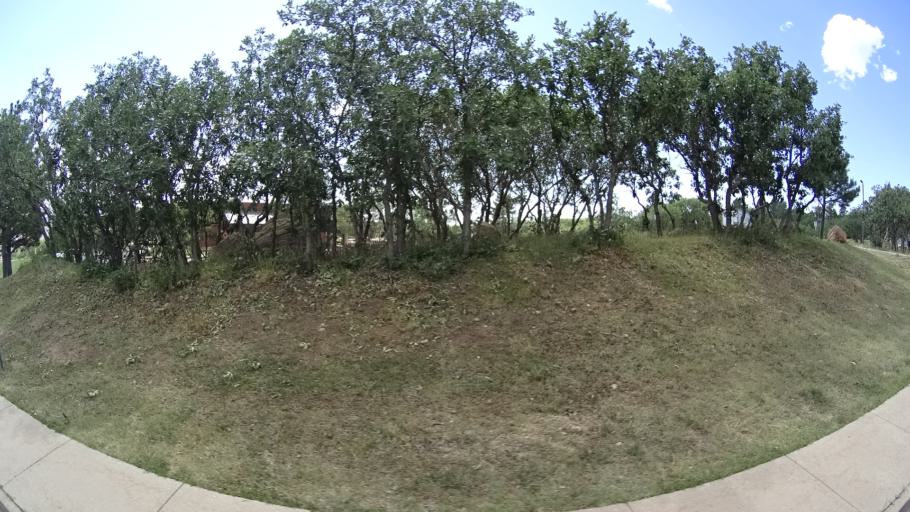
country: US
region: Colorado
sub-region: El Paso County
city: Fort Carson
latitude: 38.7603
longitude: -104.8250
